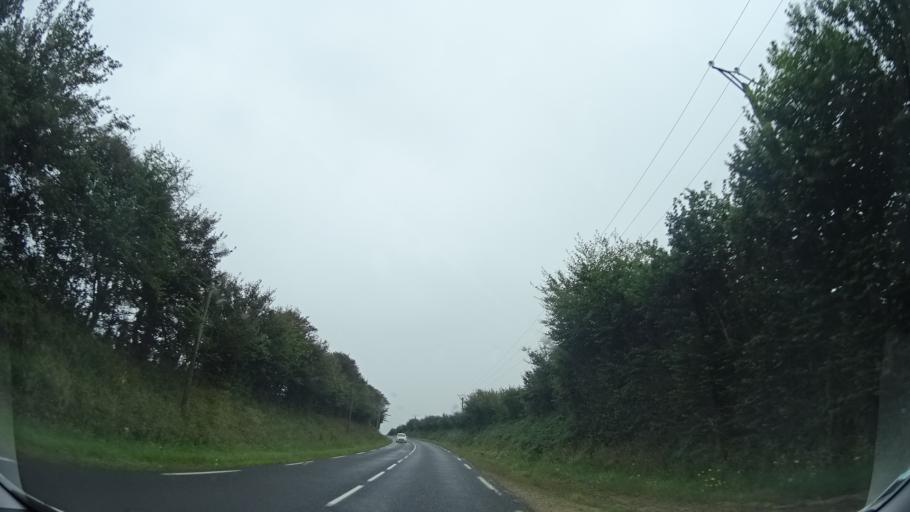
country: FR
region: Lower Normandy
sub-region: Departement de la Manche
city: Martinvast
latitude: 49.6143
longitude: -1.6931
